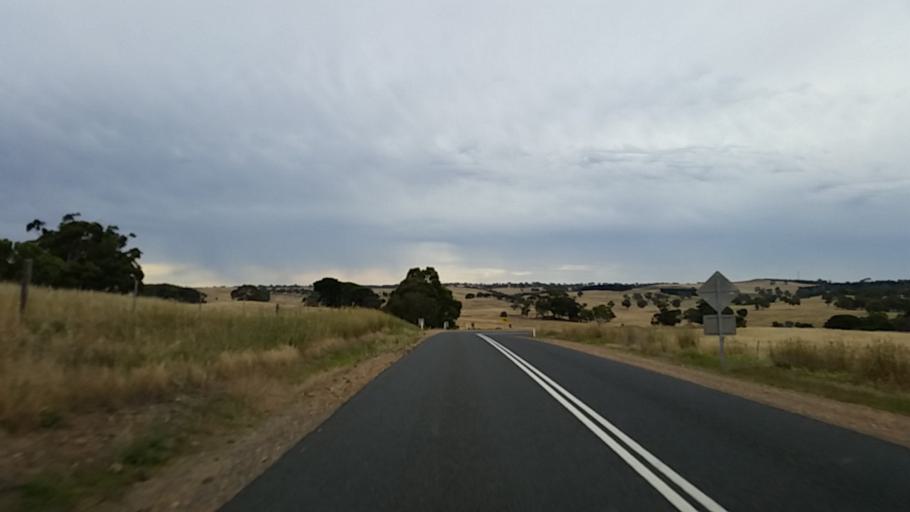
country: AU
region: South Australia
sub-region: Adelaide Hills
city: Birdwood
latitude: -34.7744
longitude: 139.1002
